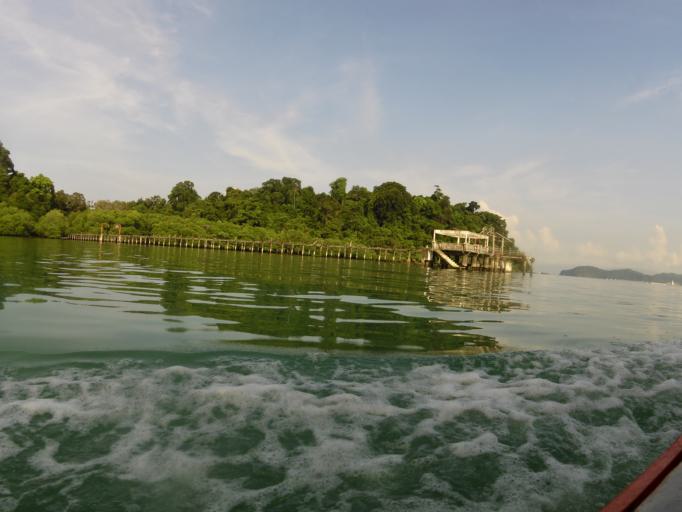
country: MY
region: Kedah
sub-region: Langkawi
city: Kuah
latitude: 6.2252
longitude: 99.7353
